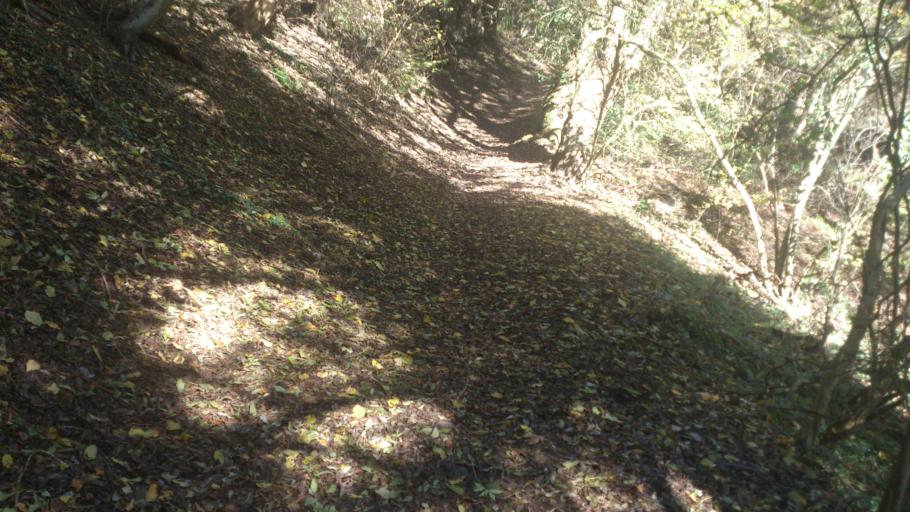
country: BE
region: Wallonia
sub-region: Province de Liege
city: Beyne-Heusay
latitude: 50.6311
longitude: 5.6768
